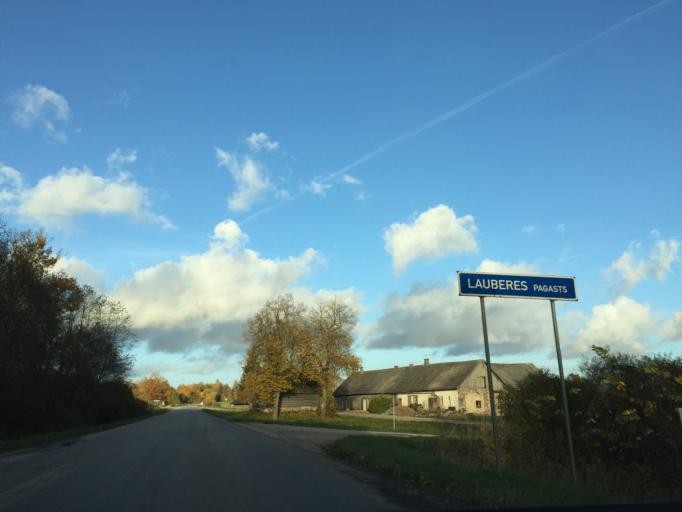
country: LV
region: Ogre
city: Jumprava
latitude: 56.7948
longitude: 25.0418
